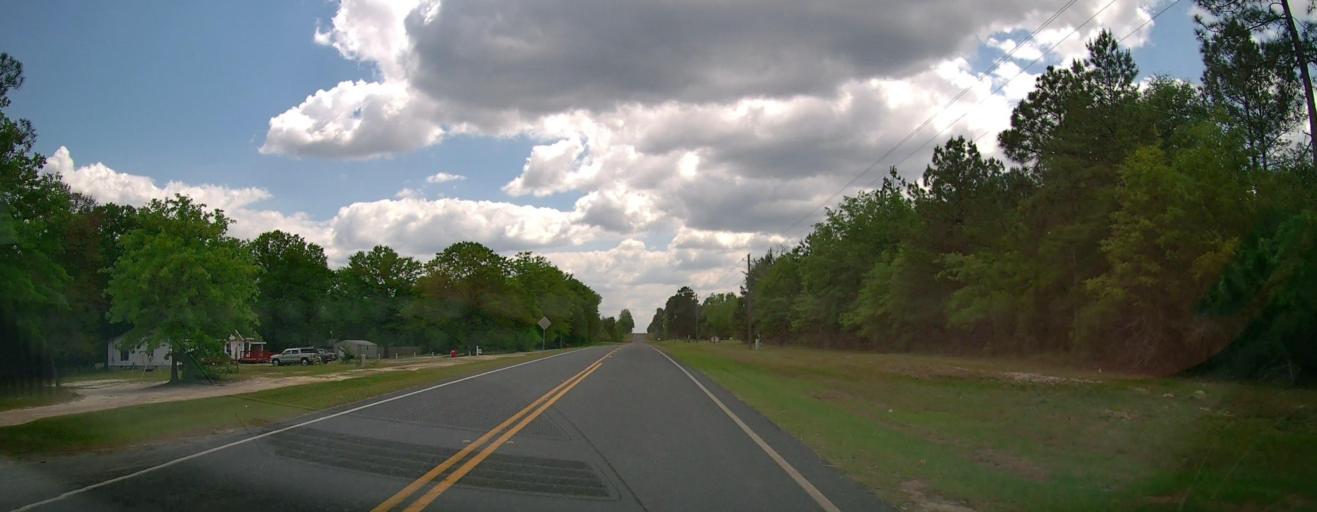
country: US
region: Georgia
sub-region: Treutlen County
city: Soperton
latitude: 32.4728
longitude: -82.6017
